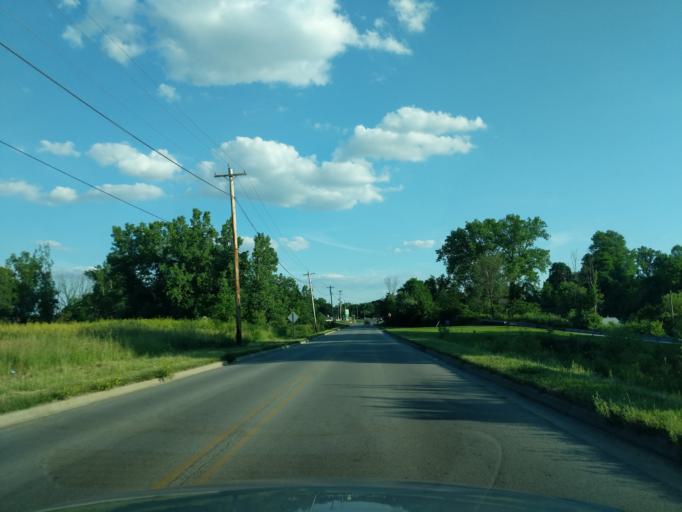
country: US
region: Indiana
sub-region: Huntington County
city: Huntington
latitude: 40.8671
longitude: -85.4709
